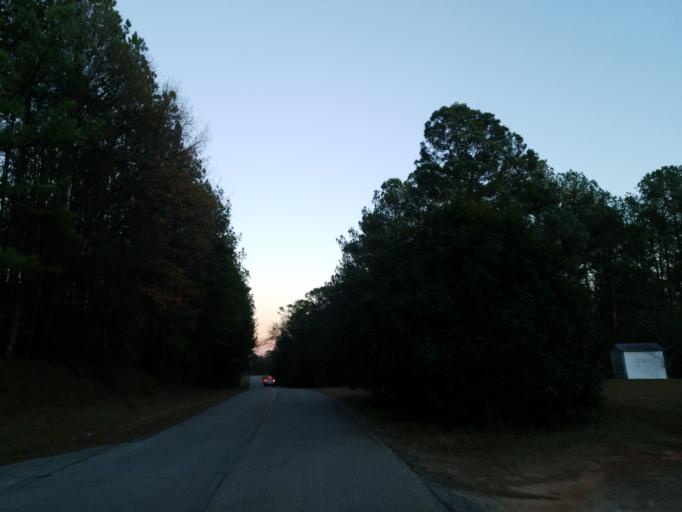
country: US
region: Georgia
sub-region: Monroe County
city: Forsyth
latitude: 33.0110
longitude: -83.8827
